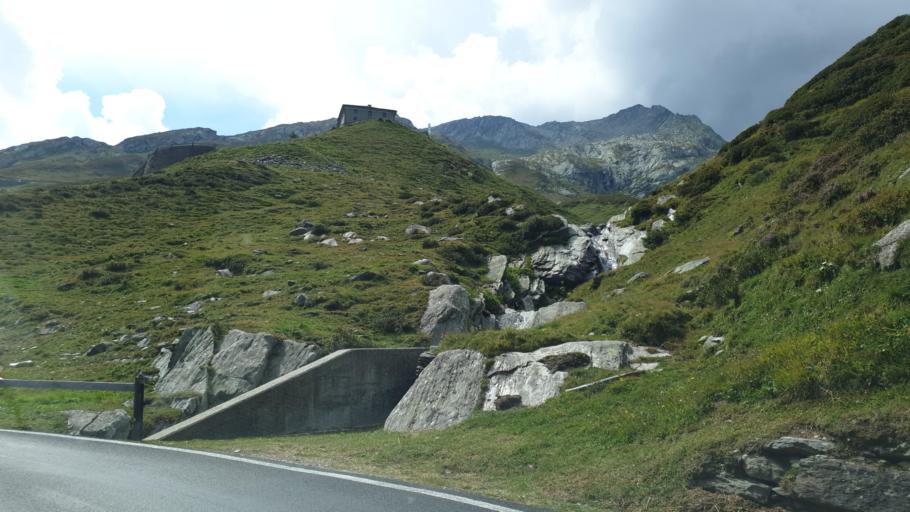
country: IT
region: Lombardy
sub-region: Provincia di Sondrio
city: Campodolcino
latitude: 46.5137
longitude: 9.3286
